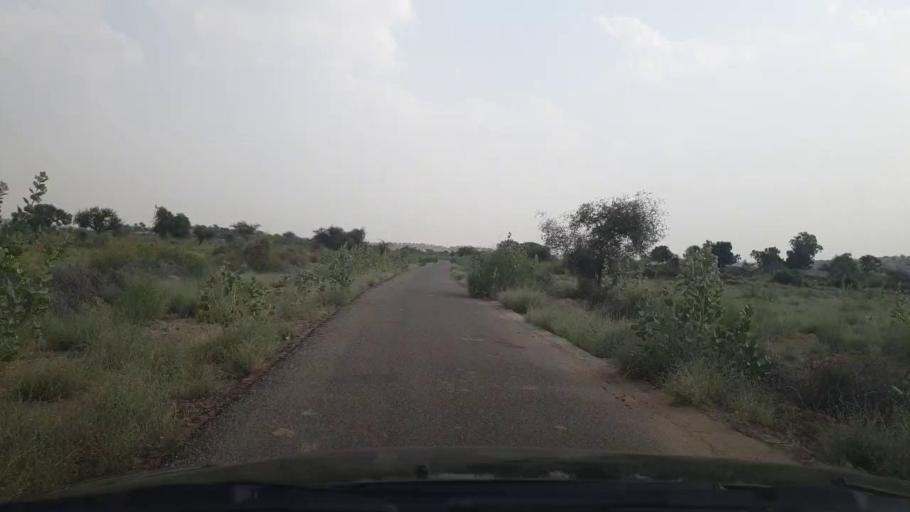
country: PK
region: Sindh
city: Islamkot
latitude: 25.0095
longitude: 70.5963
